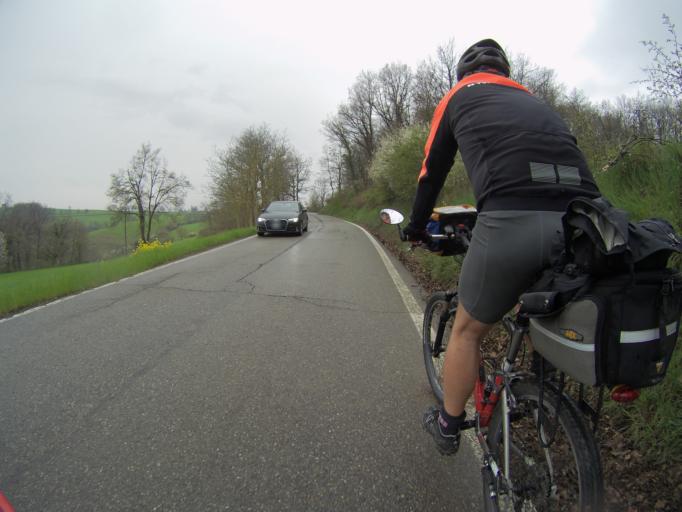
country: IT
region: Emilia-Romagna
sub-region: Provincia di Reggio Emilia
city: Ciano d'Enza
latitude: 44.5459
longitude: 10.4173
